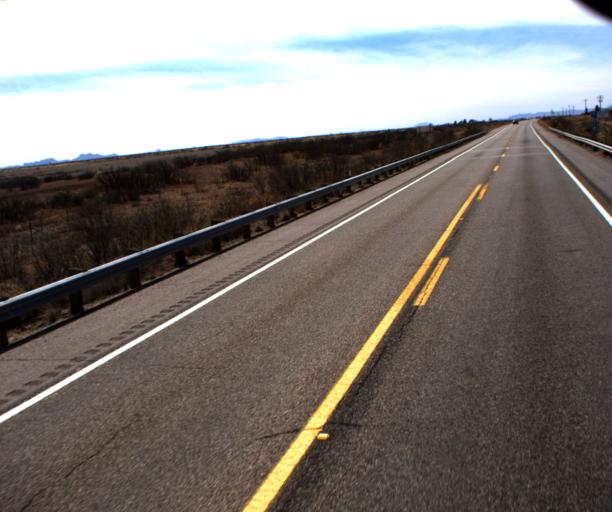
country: US
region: Arizona
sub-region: Cochise County
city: Pirtleville
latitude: 31.5943
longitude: -109.6696
